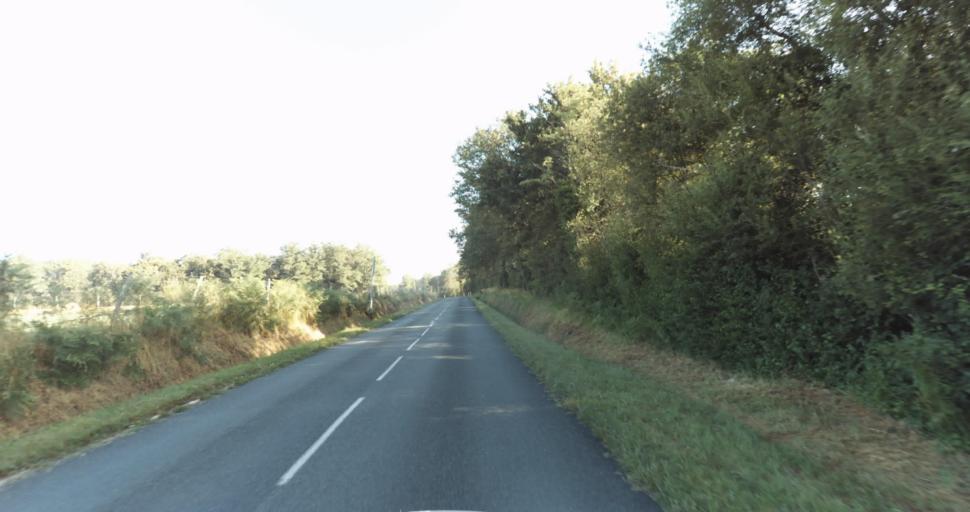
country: FR
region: Aquitaine
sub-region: Departement de la Gironde
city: Bazas
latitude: 44.4075
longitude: -0.2070
